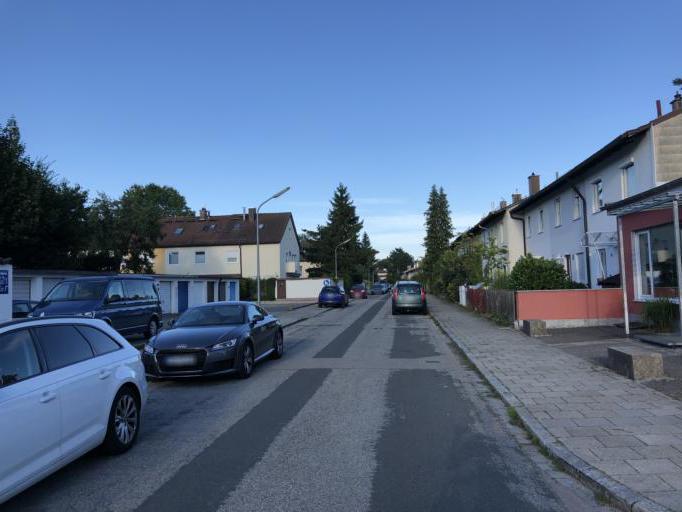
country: DE
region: Bavaria
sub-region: Upper Bavaria
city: Bogenhausen
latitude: 48.1113
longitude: 11.6241
